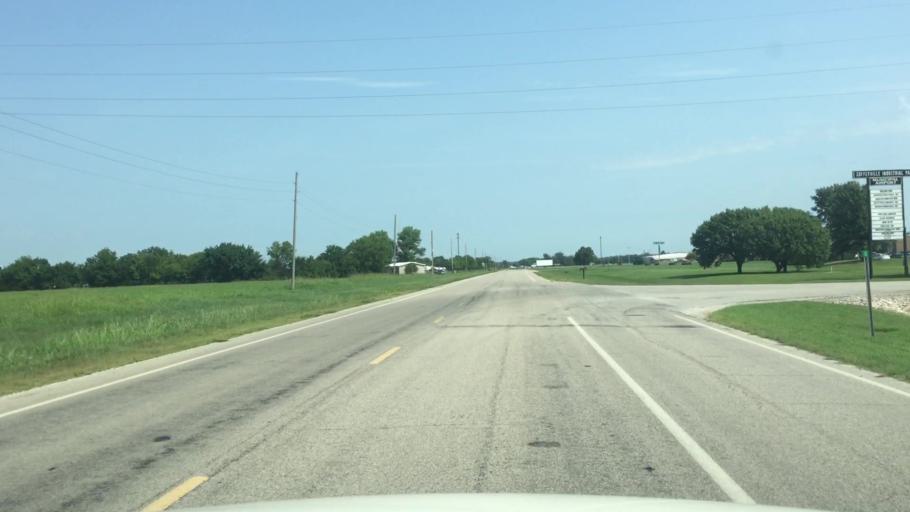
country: US
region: Kansas
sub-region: Montgomery County
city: Coffeyville
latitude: 37.0946
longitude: -95.5861
